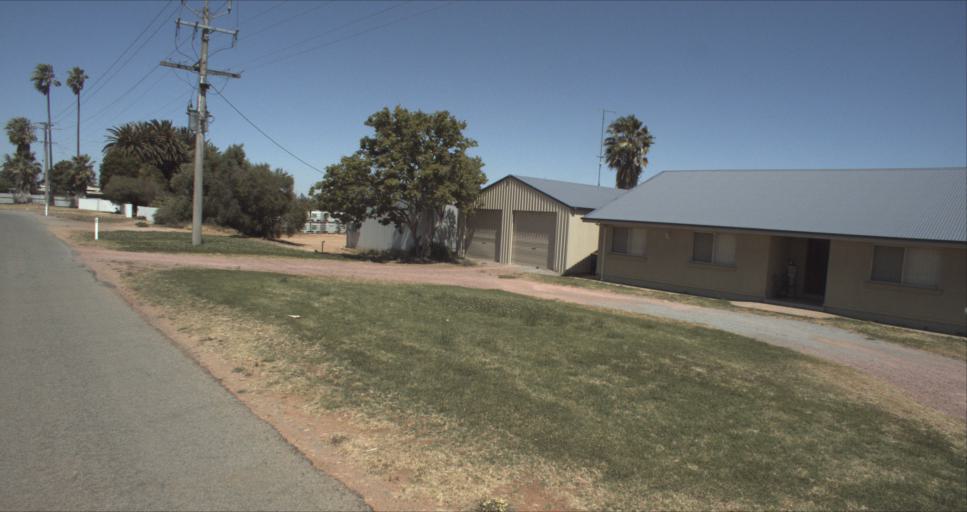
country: AU
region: New South Wales
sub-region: Leeton
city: Leeton
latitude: -34.5430
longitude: 146.3943
